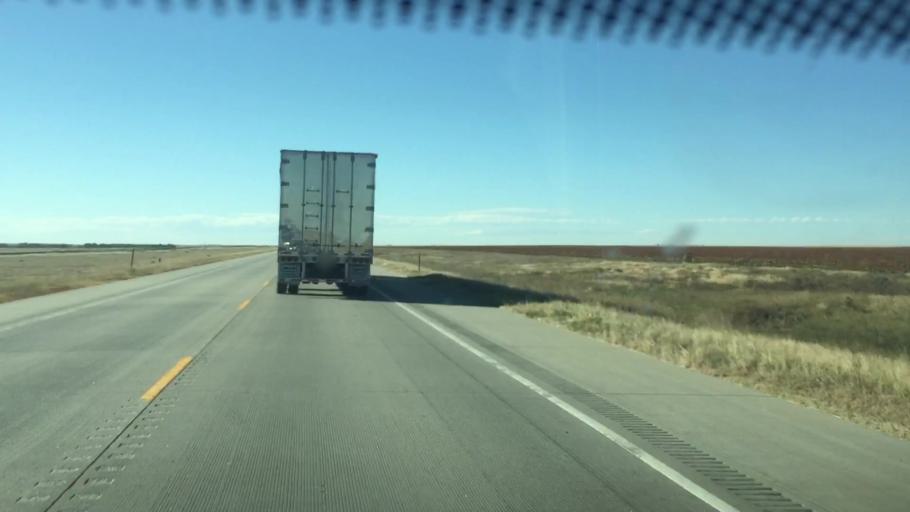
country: US
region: Colorado
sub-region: Kiowa County
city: Eads
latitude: 38.7958
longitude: -102.9462
